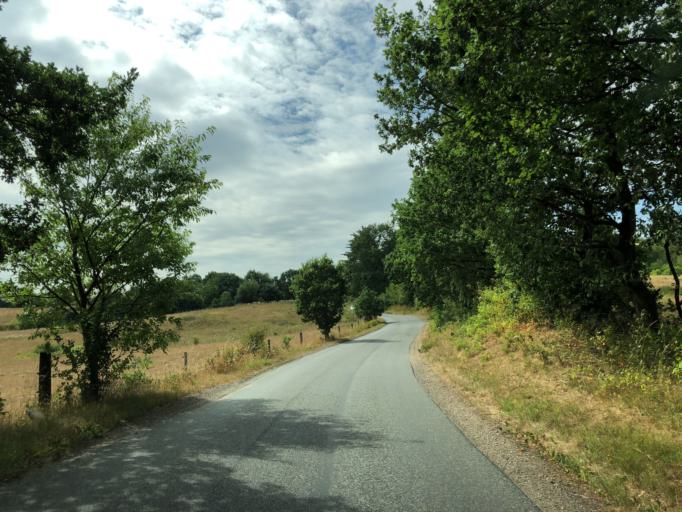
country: DK
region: South Denmark
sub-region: Vejle Kommune
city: Egtved
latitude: 55.6445
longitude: 9.2551
